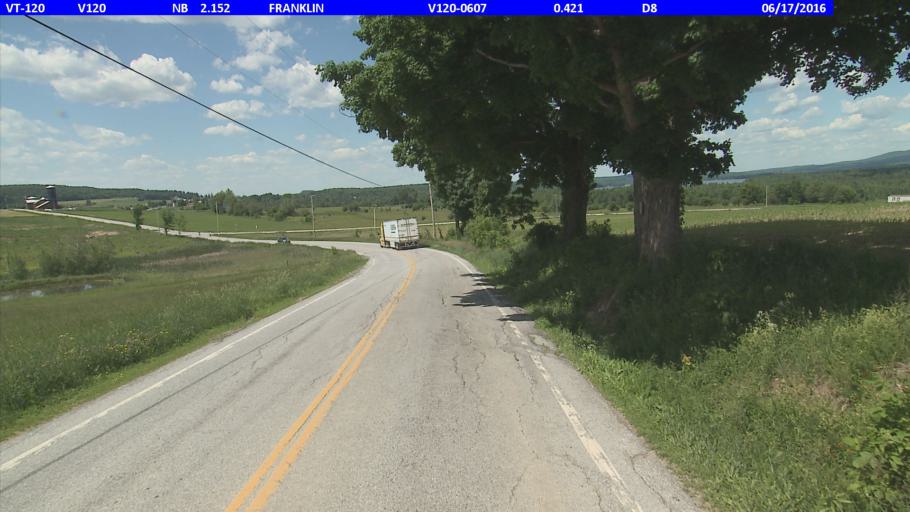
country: US
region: Vermont
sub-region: Franklin County
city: Enosburg Falls
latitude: 44.9407
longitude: -72.8983
